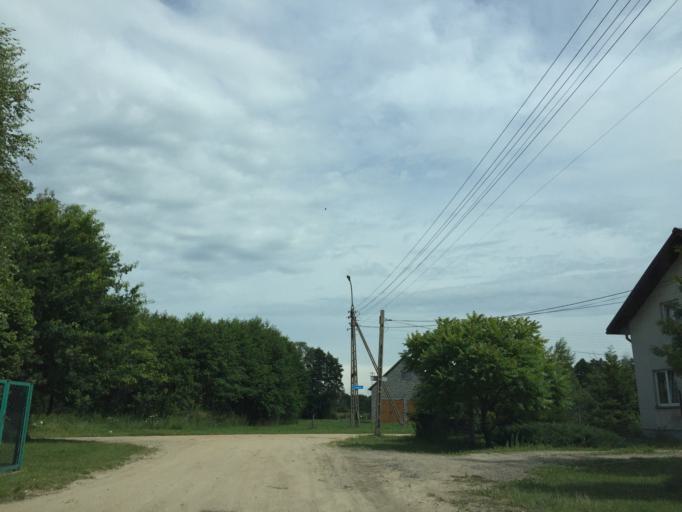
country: PL
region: Podlasie
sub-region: Powiat bielski
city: Bielsk Podlaski
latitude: 52.7429
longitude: 23.1953
